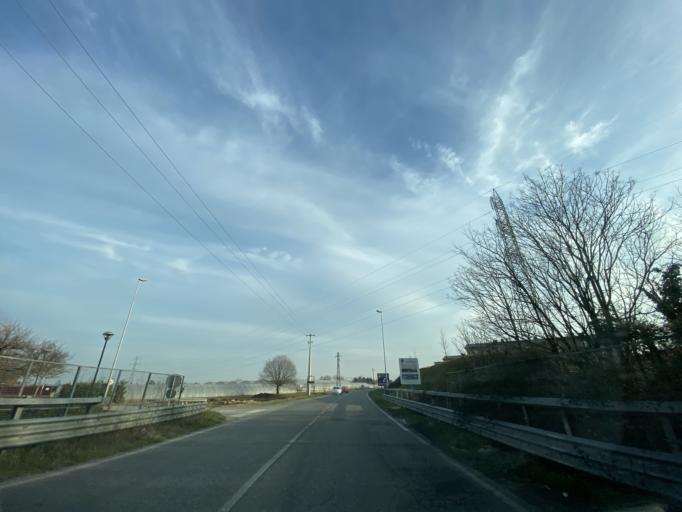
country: IT
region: Lombardy
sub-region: Citta metropolitana di Milano
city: Ronco
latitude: 45.5315
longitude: 9.3474
